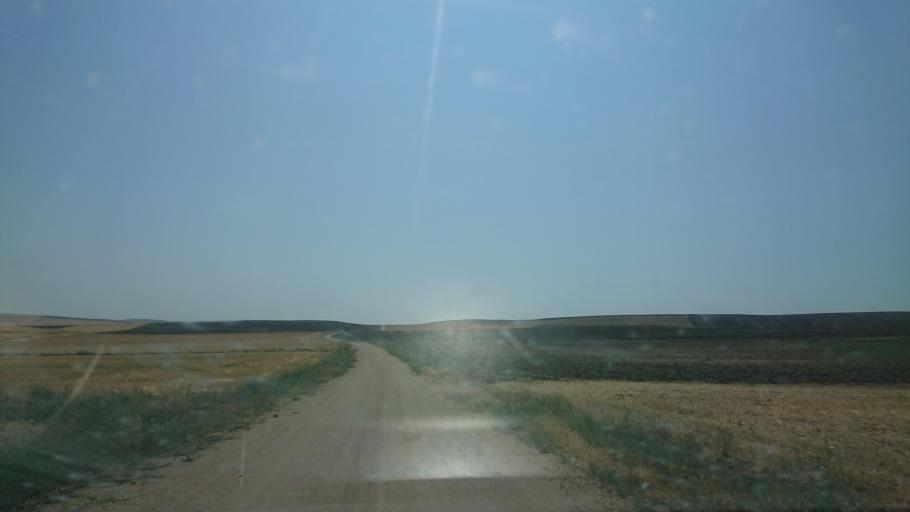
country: TR
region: Aksaray
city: Sariyahsi
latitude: 38.9562
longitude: 33.9172
